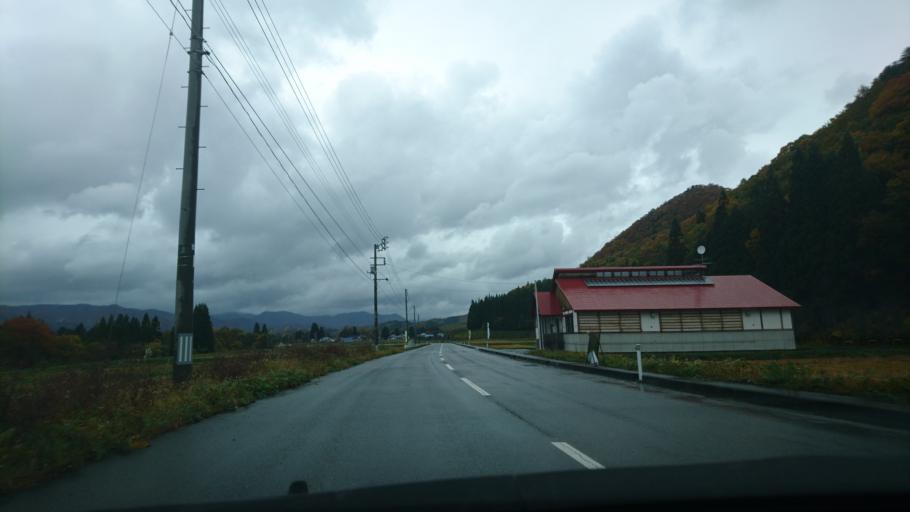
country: JP
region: Akita
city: Yokotemachi
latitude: 39.3801
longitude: 140.7663
